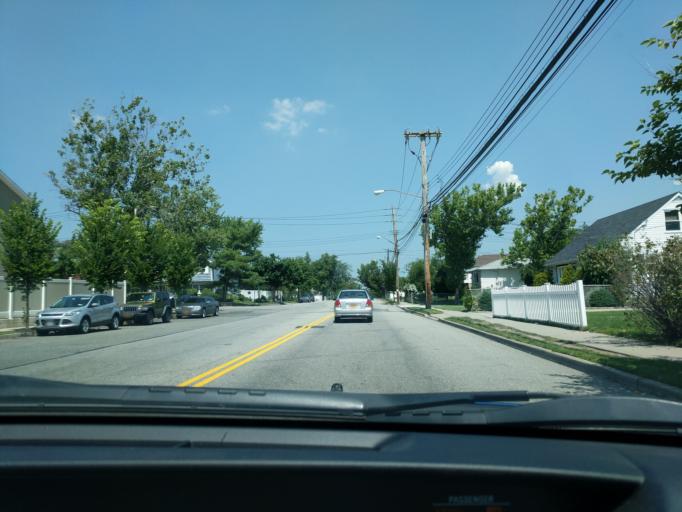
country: US
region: New Jersey
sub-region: Middlesex County
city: Carteret
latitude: 40.5394
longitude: -74.1955
